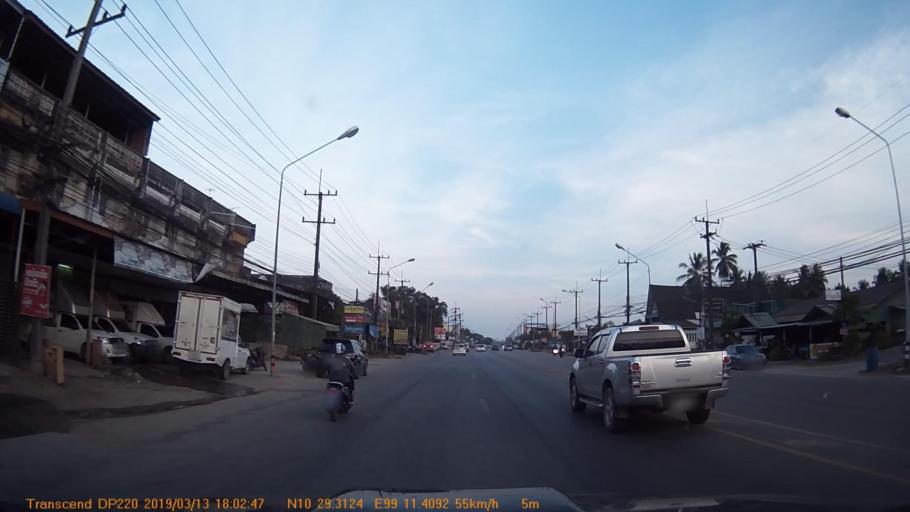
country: TH
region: Chumphon
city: Chumphon
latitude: 10.4884
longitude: 99.1903
